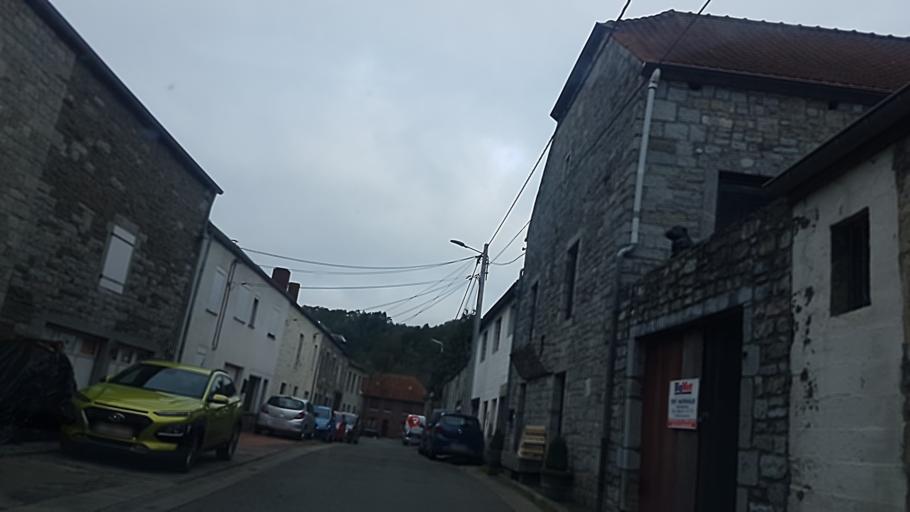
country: FR
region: Champagne-Ardenne
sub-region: Departement des Ardennes
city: Vireux-Molhain
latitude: 50.0741
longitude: 4.6088
